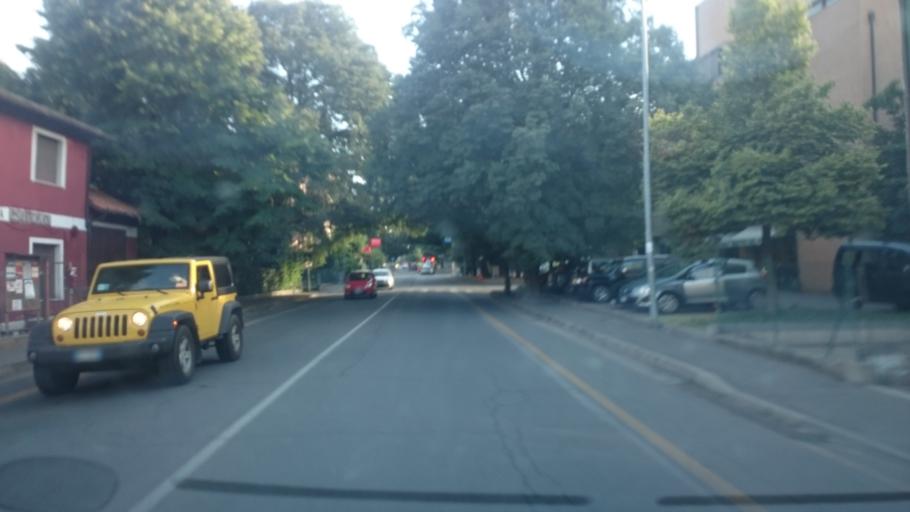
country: IT
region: Emilia-Romagna
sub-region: Provincia di Reggio Emilia
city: Reggio nell'Emilia
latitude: 44.6830
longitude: 10.6220
